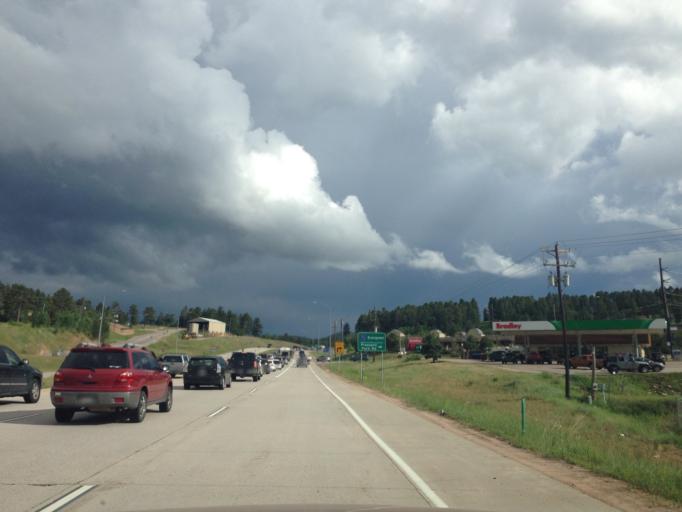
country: US
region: Colorado
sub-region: Jefferson County
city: Evergreen
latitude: 39.5215
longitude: -105.3061
